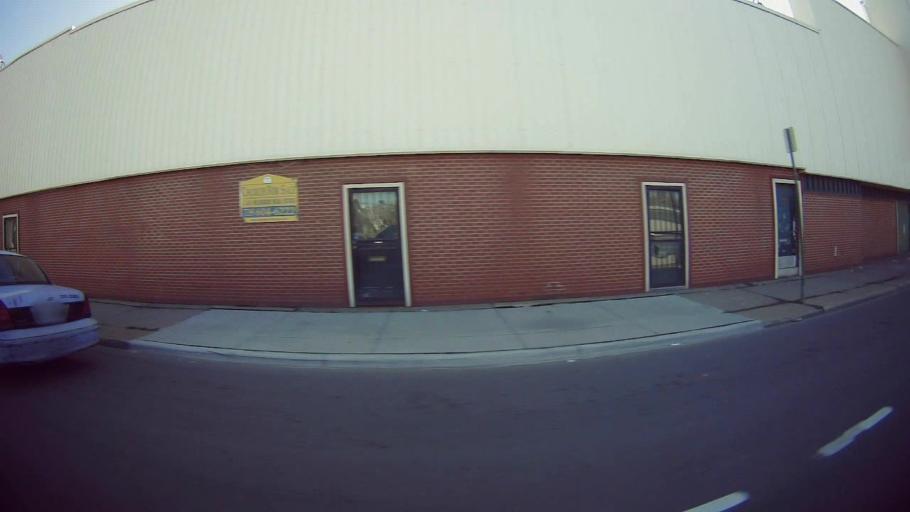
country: US
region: Michigan
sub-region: Wayne County
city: Highland Park
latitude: 42.4326
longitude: -83.0898
